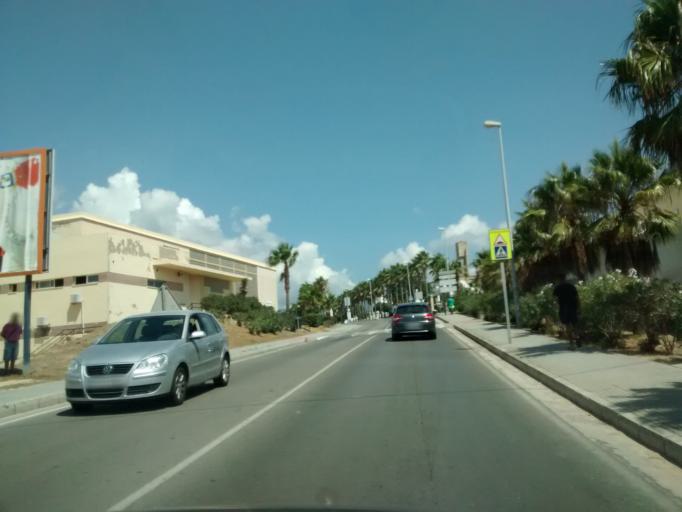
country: ES
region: Andalusia
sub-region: Provincia de Cadiz
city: Tarifa
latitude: 36.0165
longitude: -5.6017
